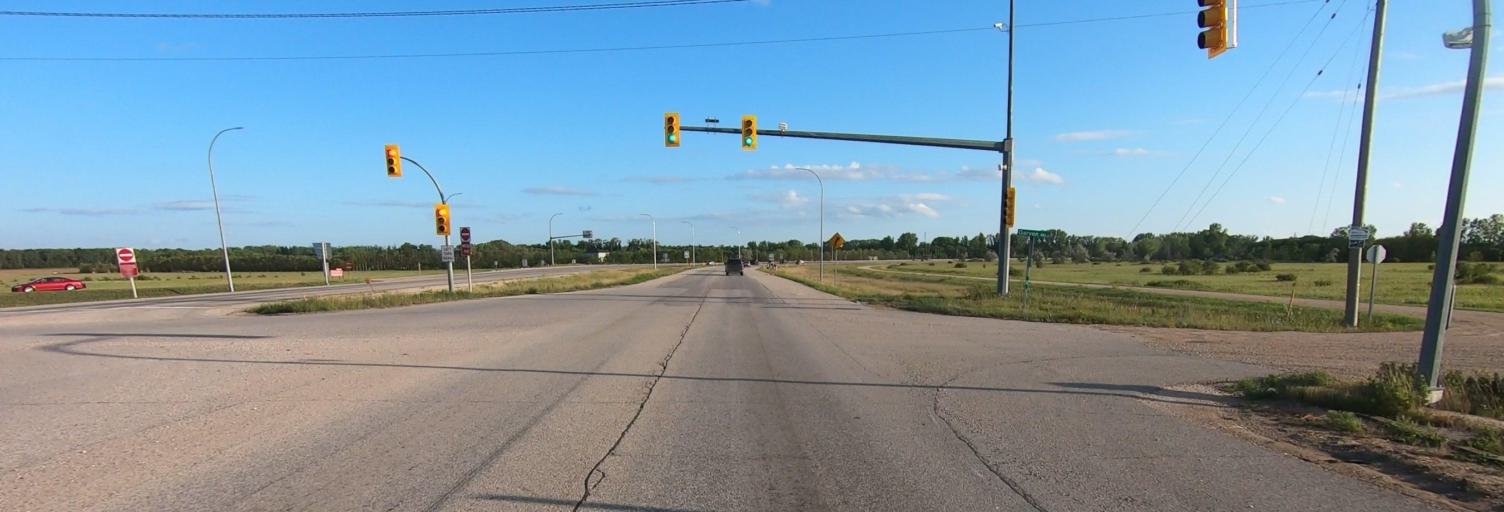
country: CA
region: Manitoba
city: Selkirk
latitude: 49.9744
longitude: -96.9726
